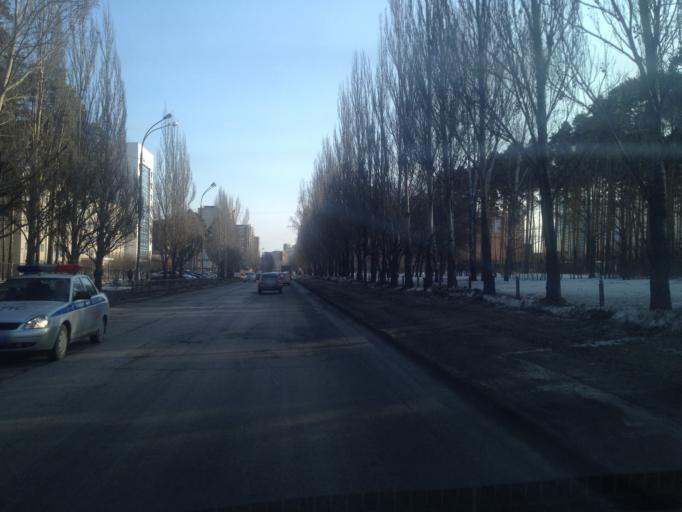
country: RU
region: Sverdlovsk
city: Sovkhoznyy
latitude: 56.8077
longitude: 60.5617
